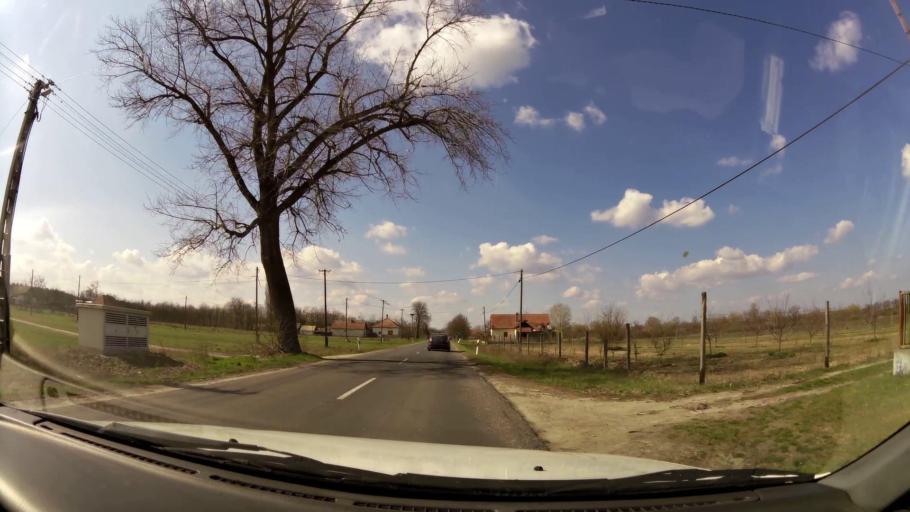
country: HU
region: Pest
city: Farmos
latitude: 47.3616
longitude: 19.8123
